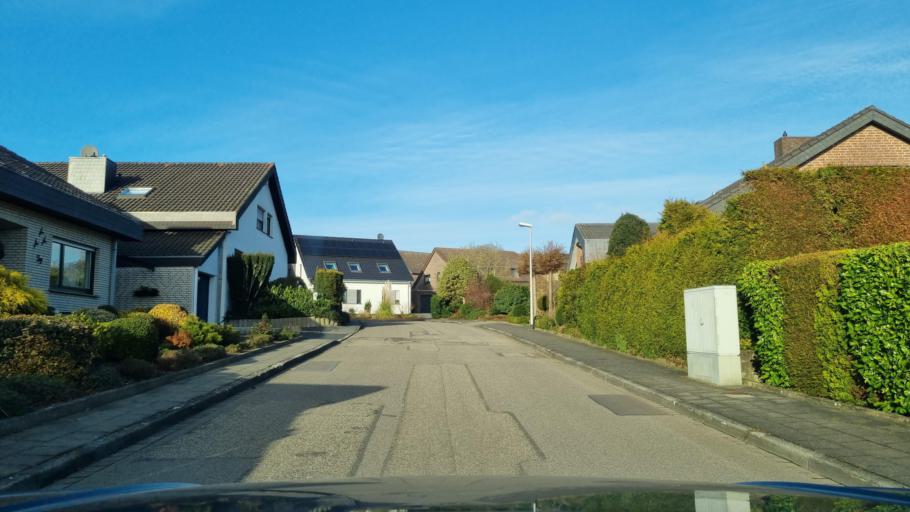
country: DE
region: North Rhine-Westphalia
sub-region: Regierungsbezirk Dusseldorf
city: Kleve
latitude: 51.7762
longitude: 6.1007
